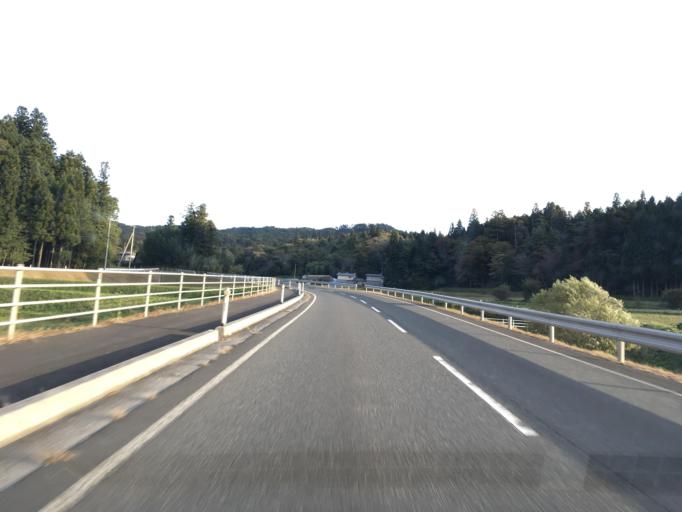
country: JP
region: Iwate
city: Mizusawa
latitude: 39.0411
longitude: 141.3736
